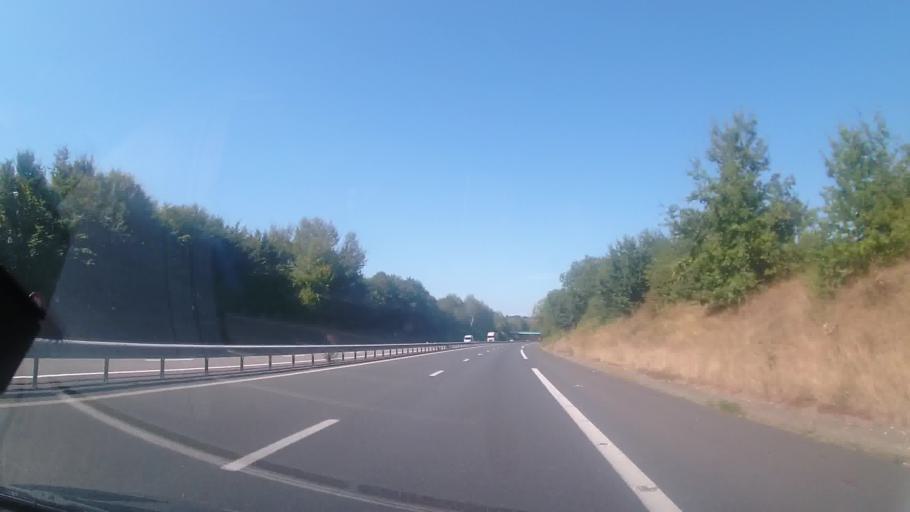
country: FR
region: Limousin
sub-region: Departement de la Correze
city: Uzerche
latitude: 45.4067
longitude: 1.5432
